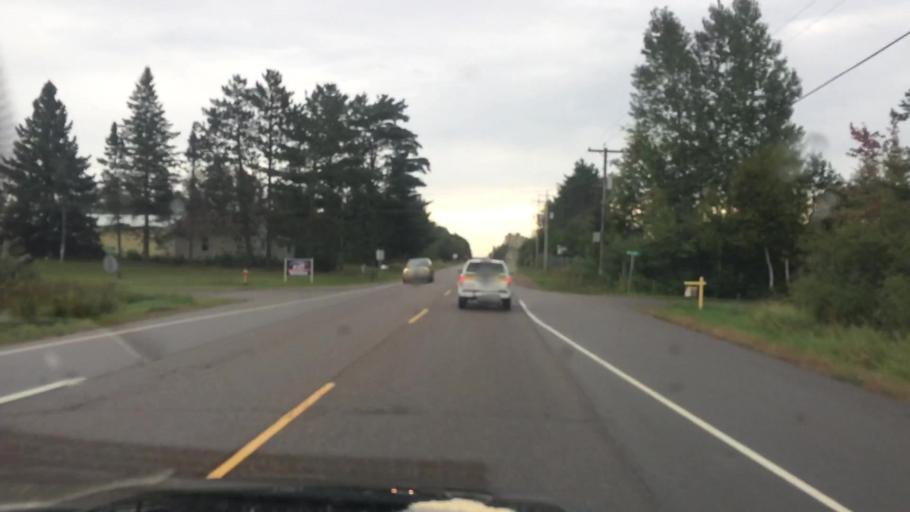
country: US
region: Wisconsin
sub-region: Lincoln County
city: Tomahawk
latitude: 45.4962
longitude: -89.7245
